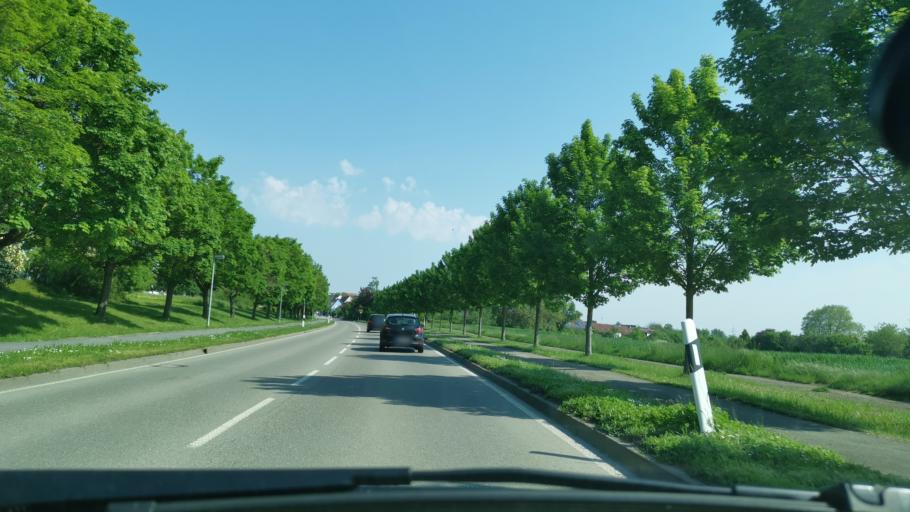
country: DE
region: Baden-Wuerttemberg
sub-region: Regierungsbezirk Stuttgart
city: Herrenberg
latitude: 48.6018
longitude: 8.8605
